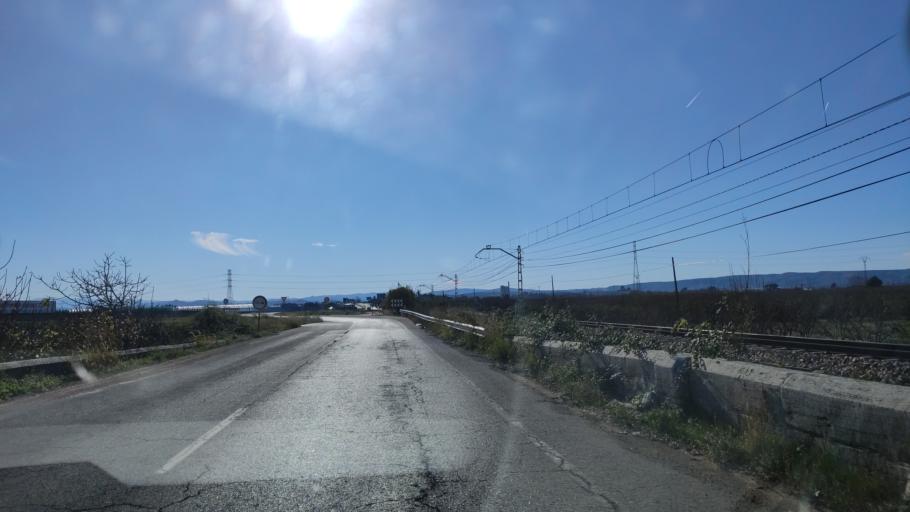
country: ES
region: Valencia
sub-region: Provincia de Valencia
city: L'Alcudia
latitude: 39.1839
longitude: -0.5121
